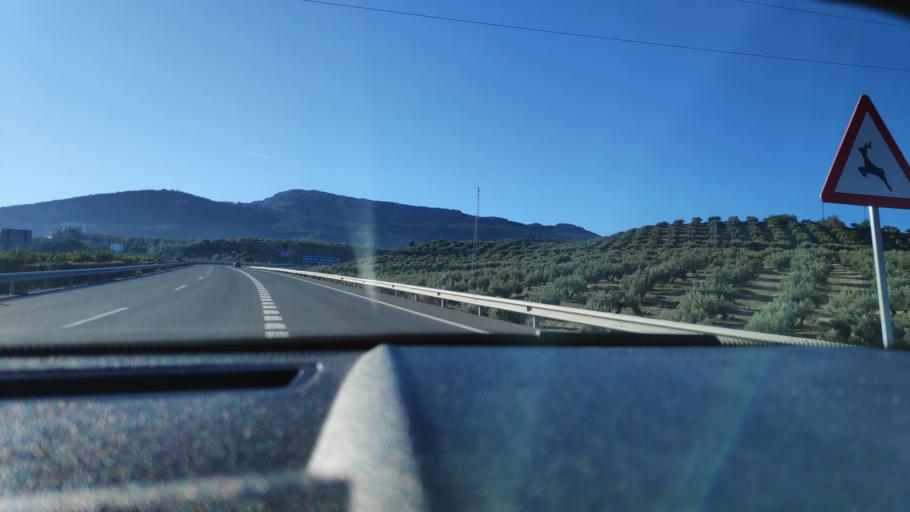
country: ES
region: Andalusia
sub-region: Provincia de Jaen
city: Jaen
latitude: 37.7938
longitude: -3.8257
